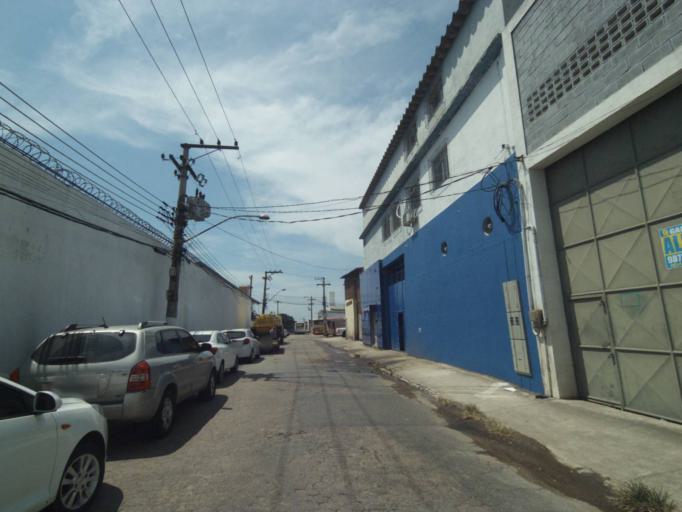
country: BR
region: Rio de Janeiro
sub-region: Duque De Caxias
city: Duque de Caxias
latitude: -22.7970
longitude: -43.2907
